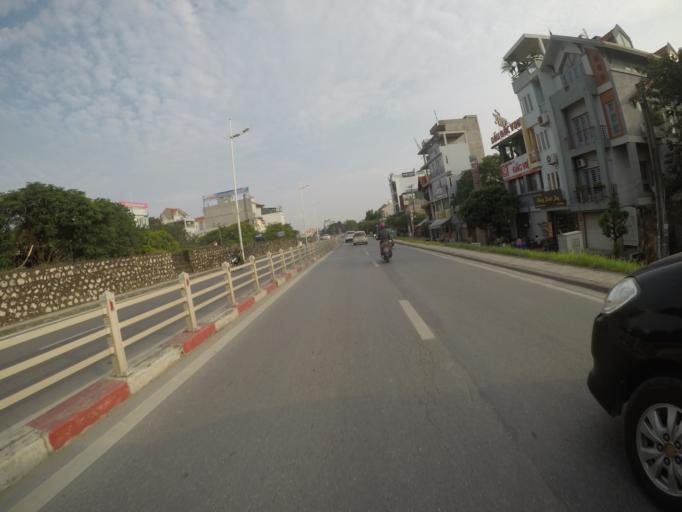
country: VN
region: Ha Noi
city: Tay Ho
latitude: 21.0780
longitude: 105.8202
